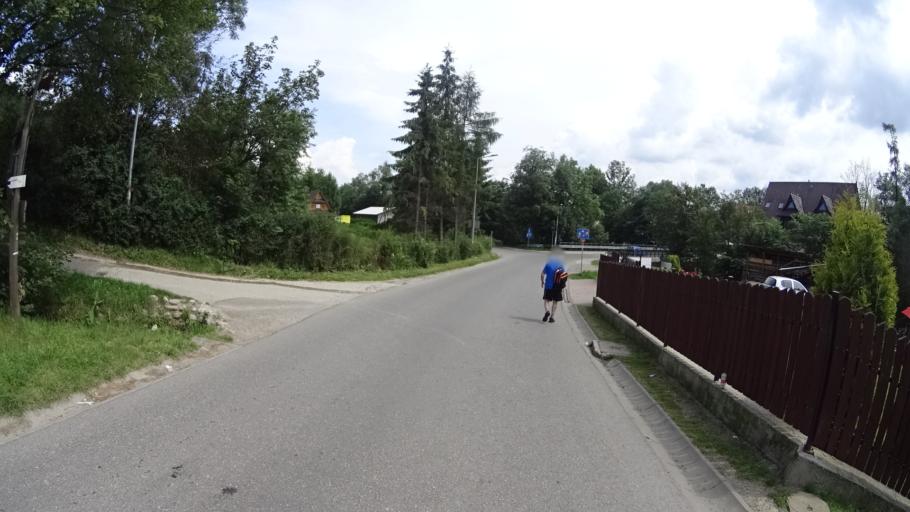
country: PL
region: Lesser Poland Voivodeship
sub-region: Powiat tatrzanski
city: Poronin
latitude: 49.3229
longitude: 19.9848
